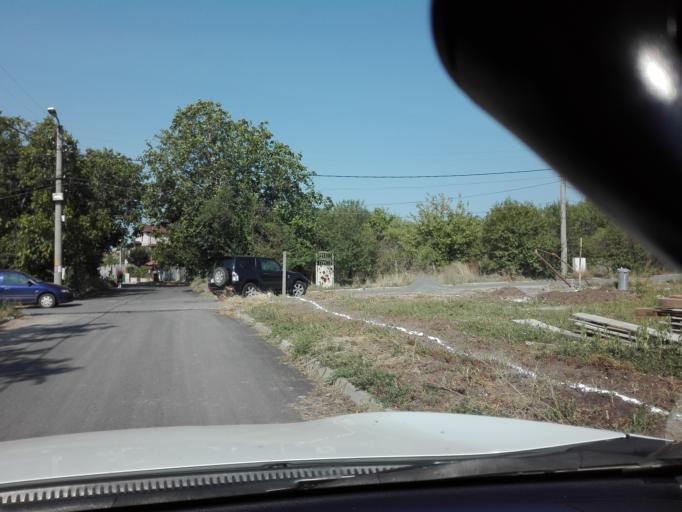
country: BG
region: Burgas
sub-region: Obshtina Kameno
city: Kameno
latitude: 42.6308
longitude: 27.3954
